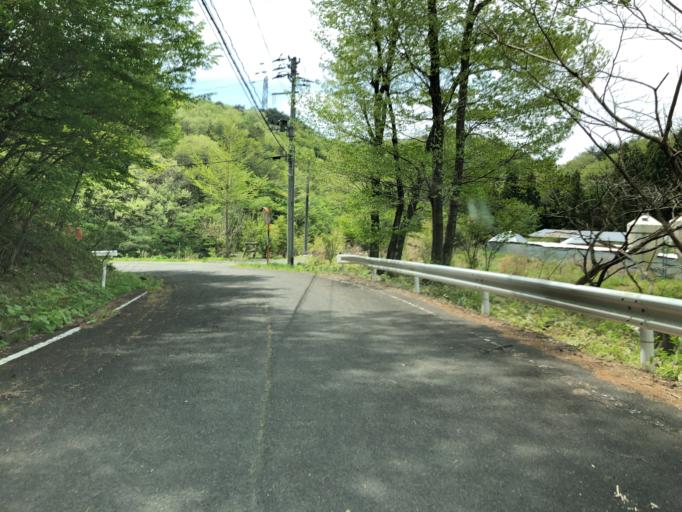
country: JP
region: Miyagi
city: Marumori
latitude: 37.7066
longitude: 140.7795
